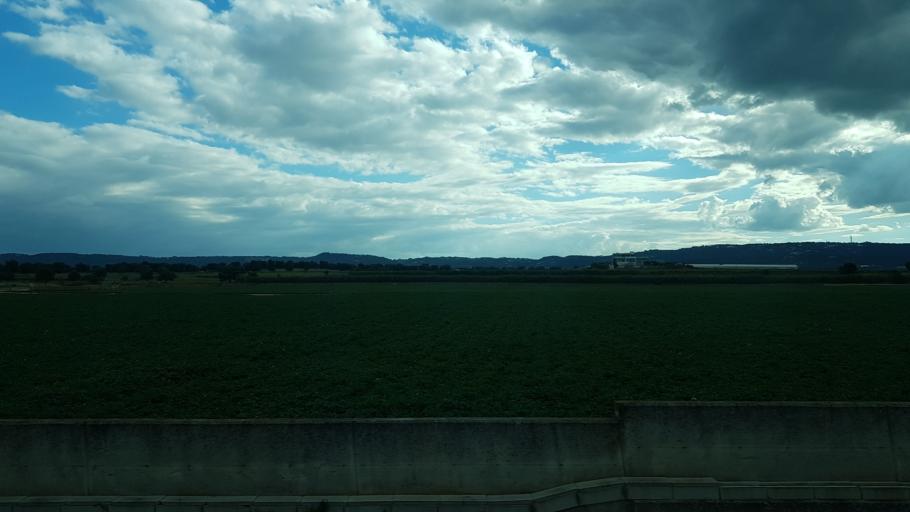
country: IT
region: Apulia
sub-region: Provincia di Brindisi
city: Fasano
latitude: 40.8458
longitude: 17.3946
